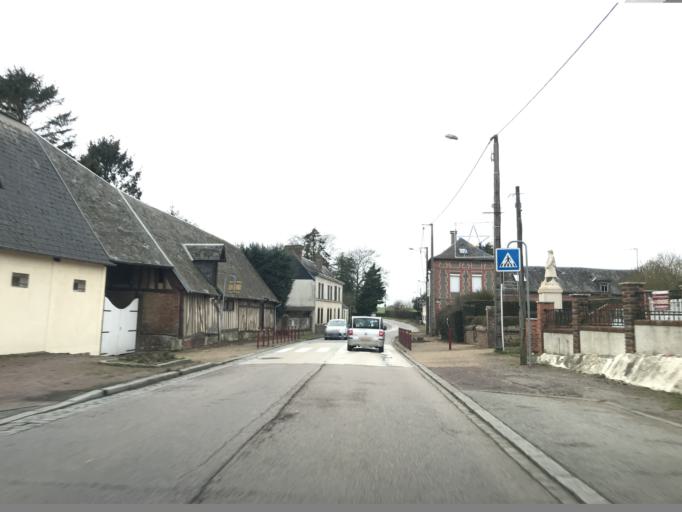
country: FR
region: Haute-Normandie
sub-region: Departement de l'Eure
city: Fleury-sur-Andelle
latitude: 49.3868
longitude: 1.3058
